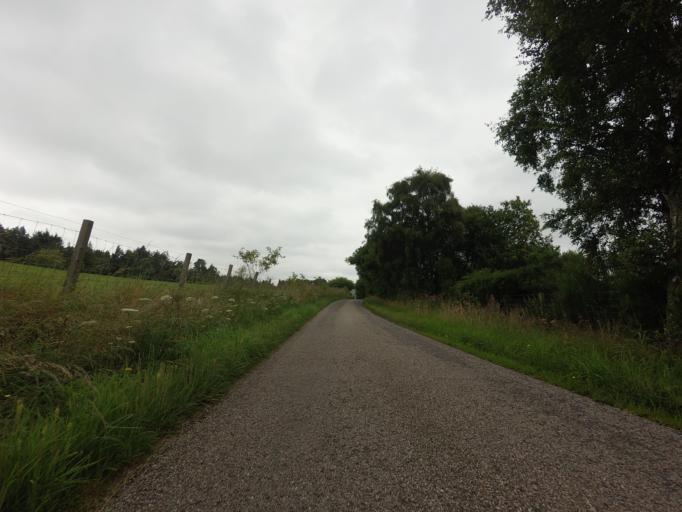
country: GB
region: Scotland
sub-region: Highland
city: Evanton
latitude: 57.9081
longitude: -4.3955
